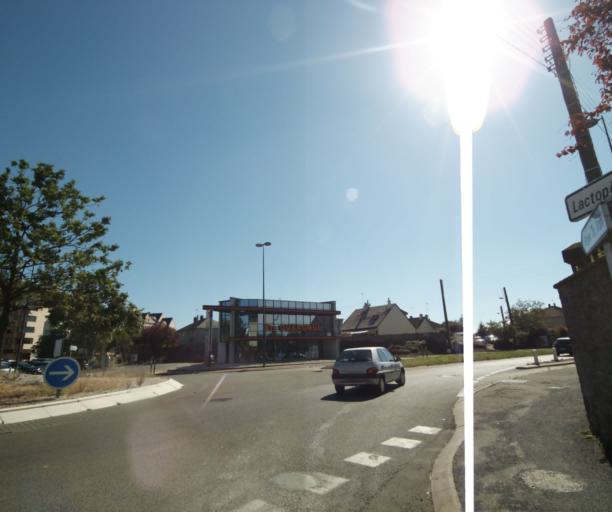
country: FR
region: Pays de la Loire
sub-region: Departement de la Mayenne
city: Laval
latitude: 48.0609
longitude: -0.7553
